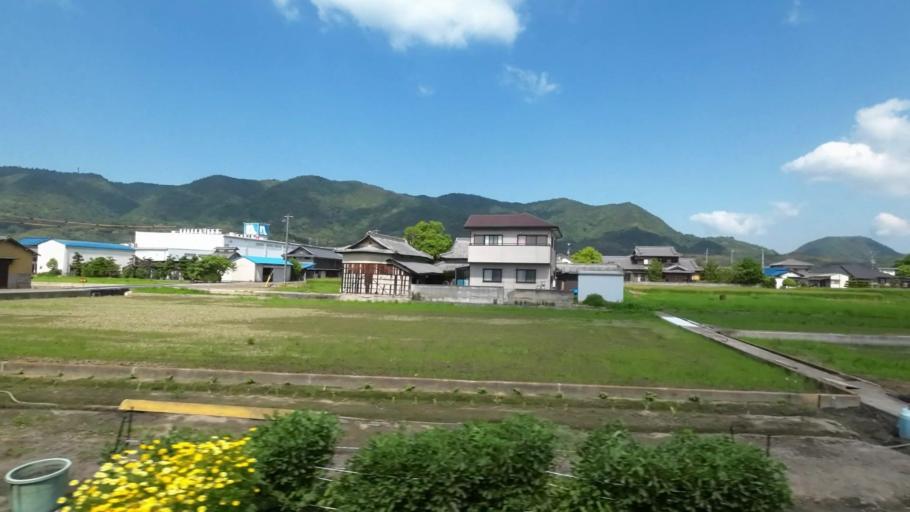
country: JP
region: Kagawa
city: Kan'onjicho
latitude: 34.1721
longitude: 133.6920
